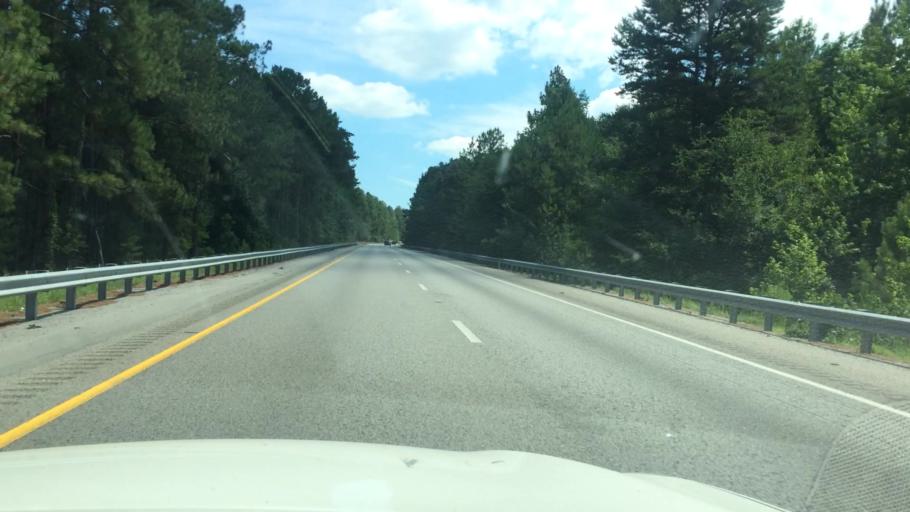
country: US
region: South Carolina
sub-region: Aiken County
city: Aiken
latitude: 33.6984
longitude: -81.6064
